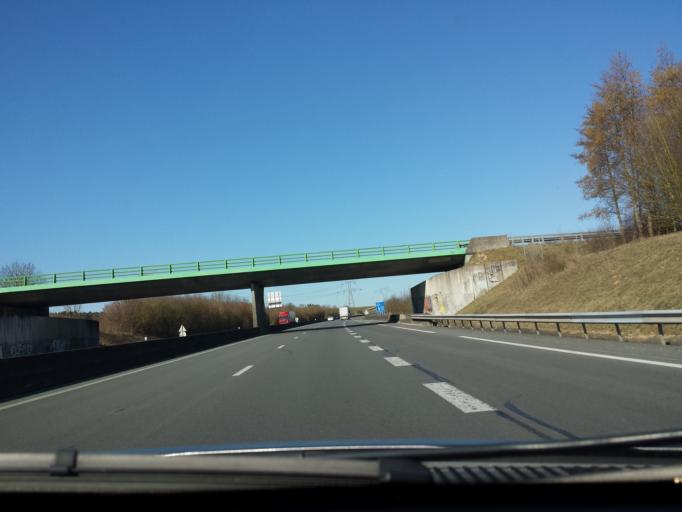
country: FR
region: Picardie
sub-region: Departement de la Somme
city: Saleux
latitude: 49.8621
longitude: 2.2182
